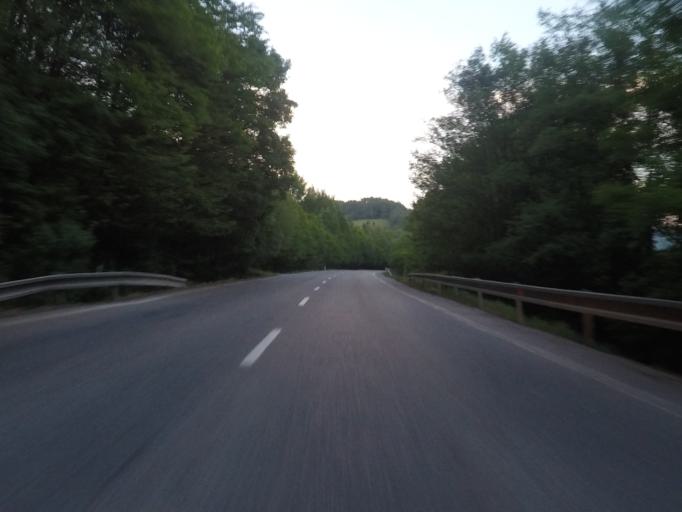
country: SK
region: Banskobystricky
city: Tisovec
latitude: 48.5232
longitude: 19.9457
